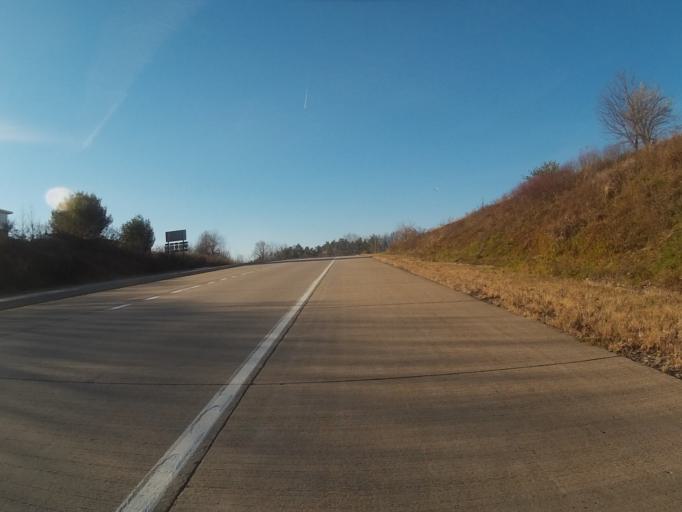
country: US
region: Pennsylvania
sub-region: Centre County
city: Houserville
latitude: 40.8334
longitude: -77.8404
